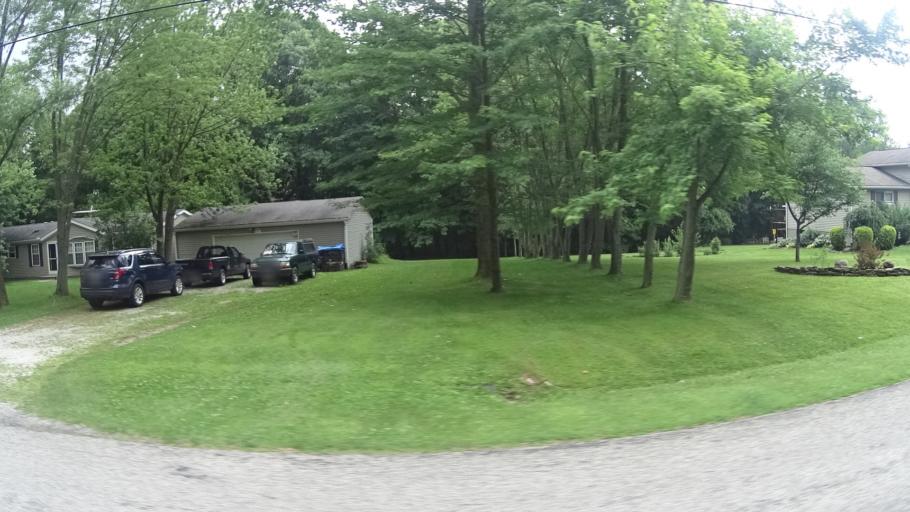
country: US
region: Ohio
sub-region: Huron County
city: Wakeman
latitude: 41.3107
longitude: -82.4813
